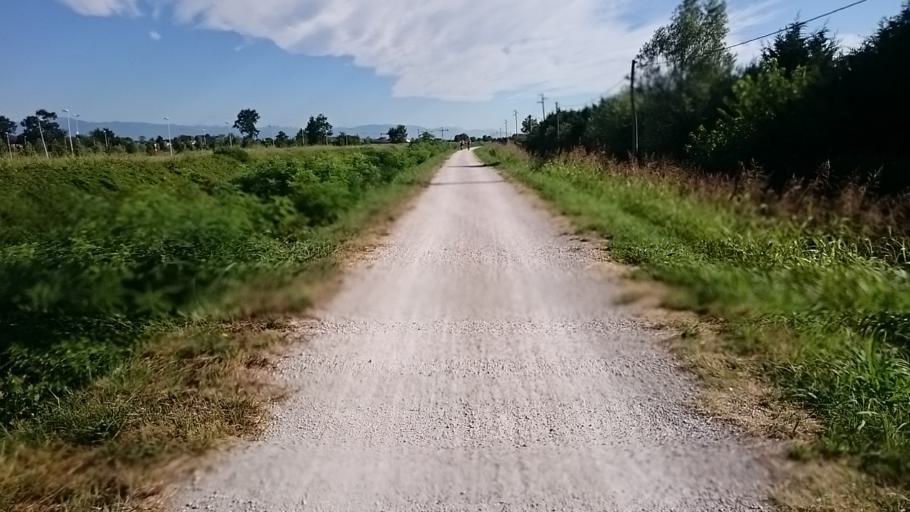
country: IT
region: Veneto
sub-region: Provincia di Padova
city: Borgoricco-San Michele delle Badesse-Sant'Eufemia
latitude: 45.5386
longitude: 11.9262
